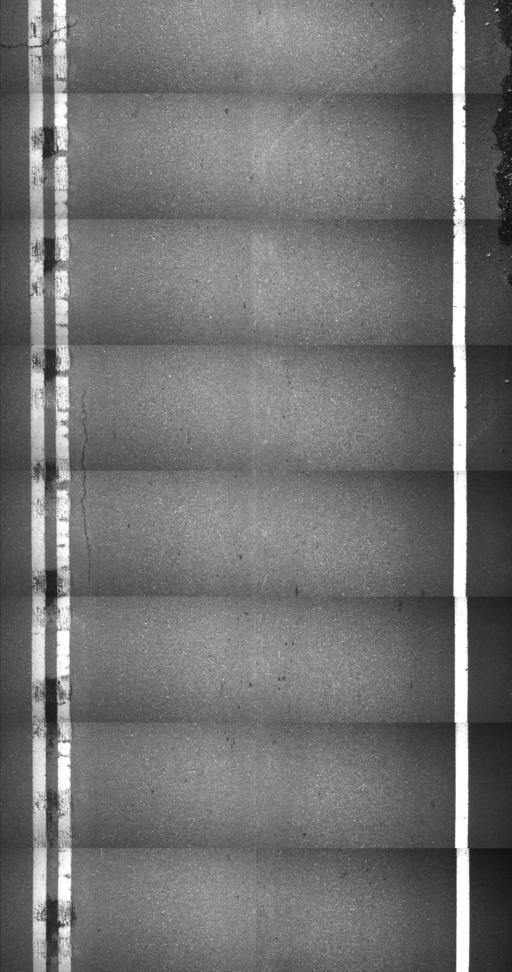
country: US
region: New Hampshire
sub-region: Cheshire County
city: Westmoreland
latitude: 43.0346
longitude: -72.4667
